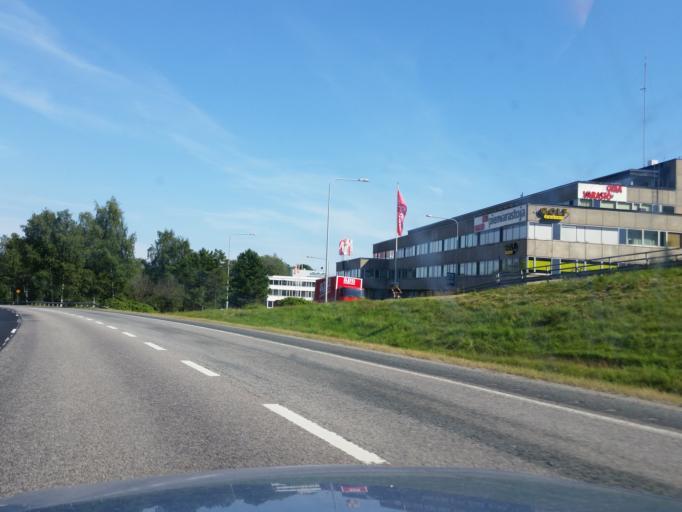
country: FI
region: Uusimaa
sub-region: Helsinki
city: Teekkarikylae
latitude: 60.1623
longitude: 24.8645
